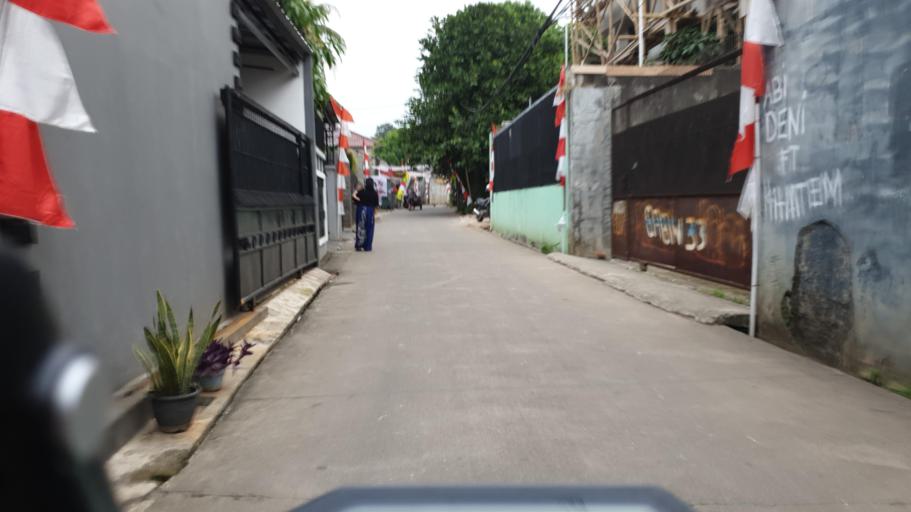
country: ID
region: West Java
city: Pamulang
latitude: -6.3211
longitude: 106.7703
